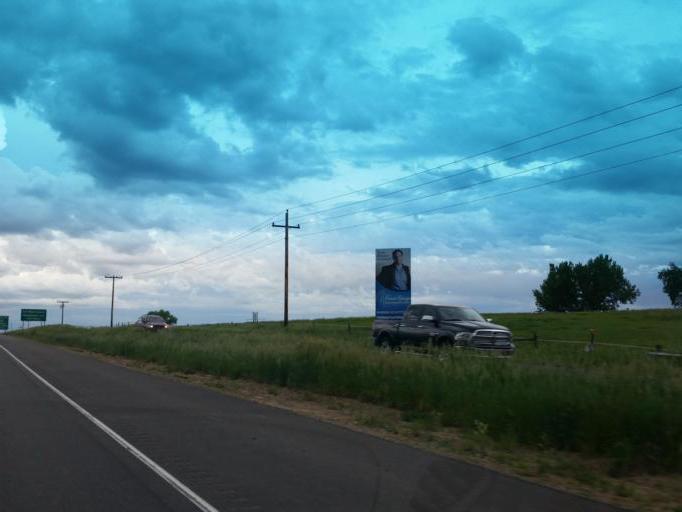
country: US
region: Colorado
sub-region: Weld County
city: Windsor
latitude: 40.4997
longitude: -104.9920
